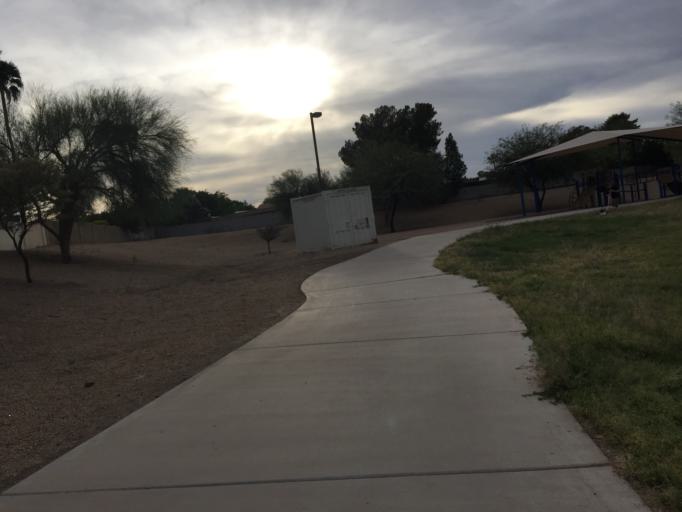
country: US
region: Arizona
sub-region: Maricopa County
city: Paradise Valley
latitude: 33.5745
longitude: -112.0097
